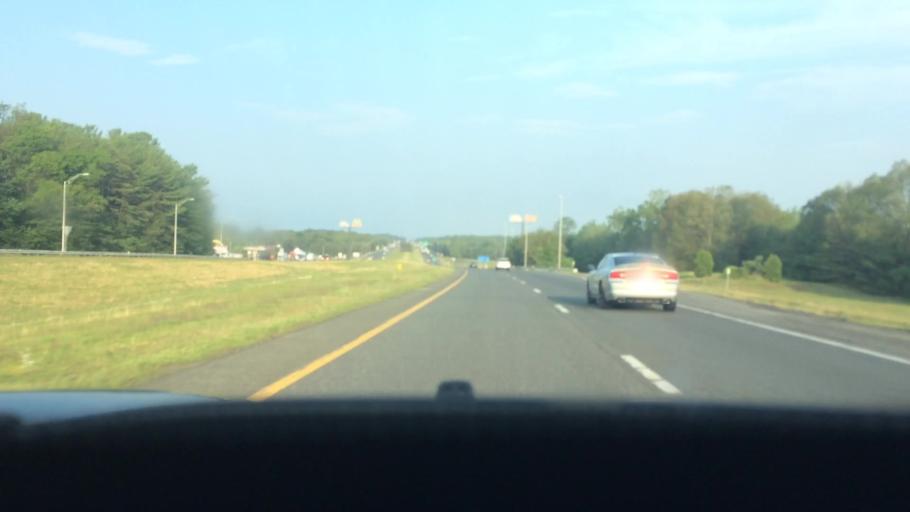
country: US
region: Massachusetts
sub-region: Hampden County
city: Ludlow
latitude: 42.1705
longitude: -72.4492
